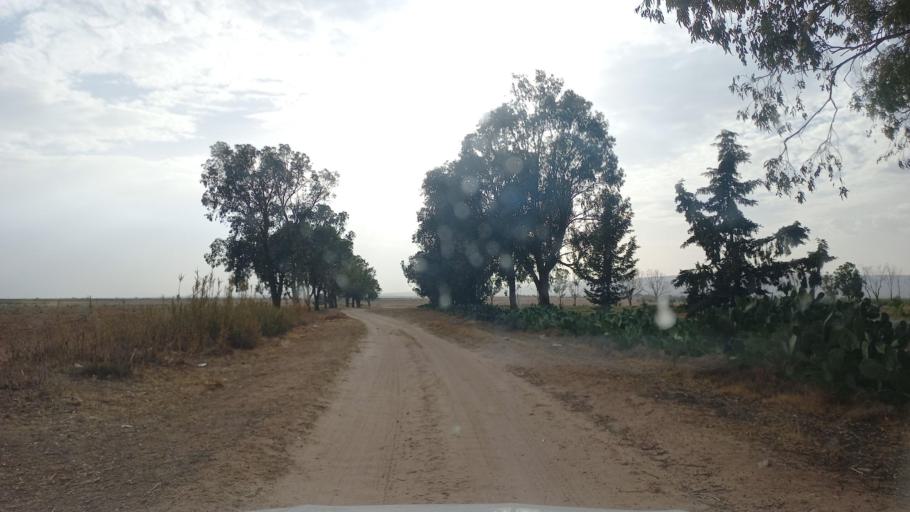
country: TN
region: Al Qasrayn
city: Kasserine
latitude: 35.2930
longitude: 9.0537
